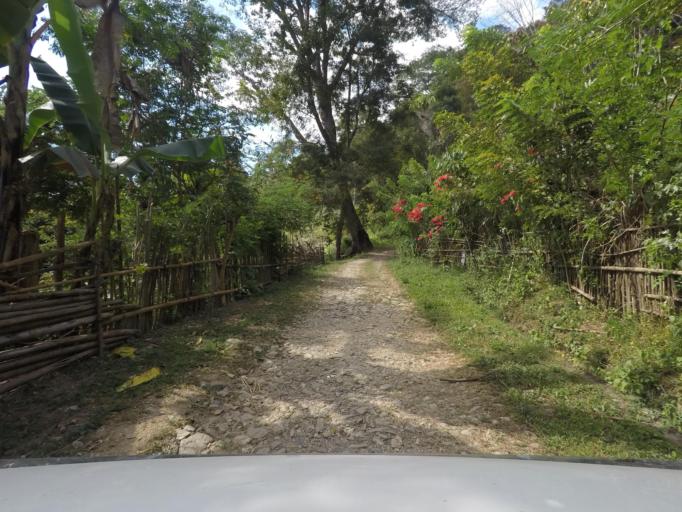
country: TL
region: Ermera
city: Gleno
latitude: -8.7189
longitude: 125.3077
